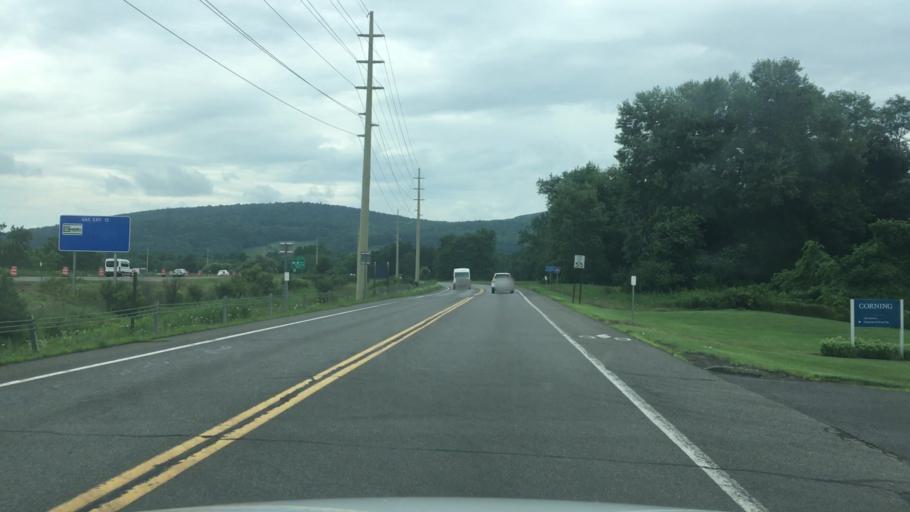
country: US
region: New York
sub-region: Otsego County
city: West End
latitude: 42.4439
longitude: -75.0941
